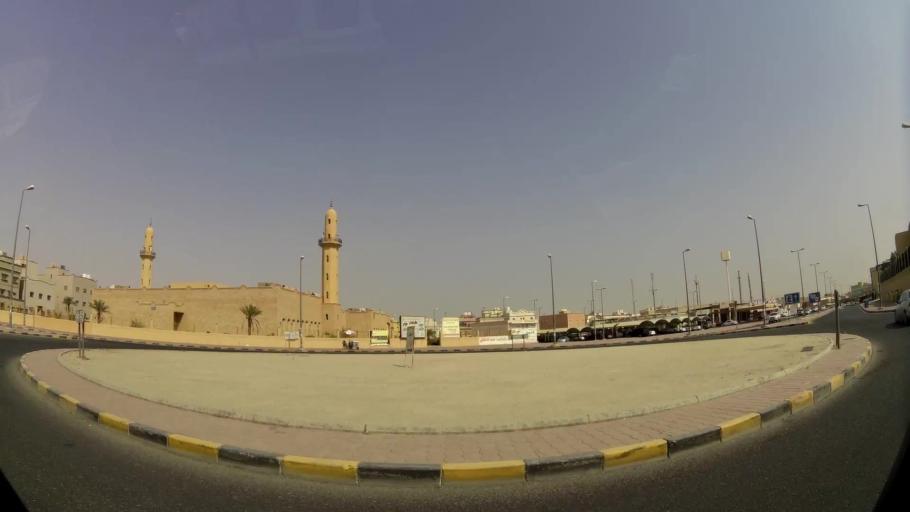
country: KW
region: Muhafazat al Jahra'
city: Al Jahra'
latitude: 29.3066
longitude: 47.6942
